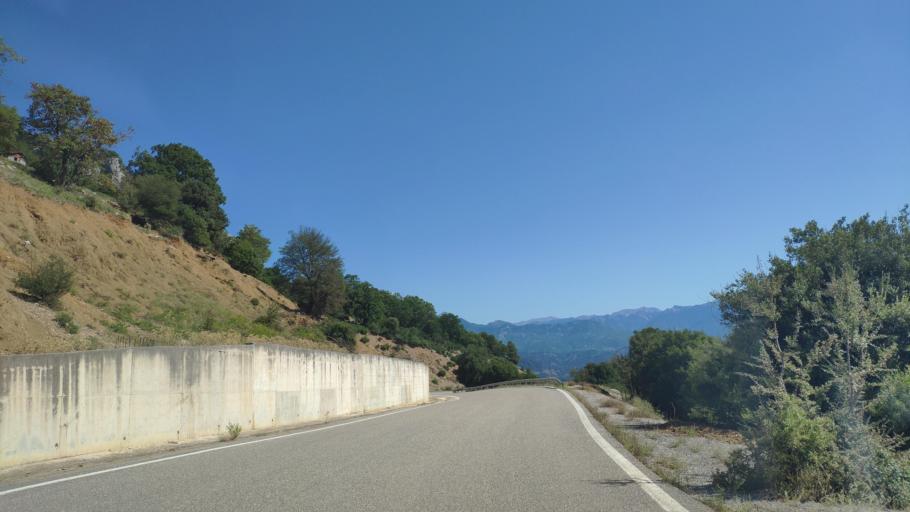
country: GR
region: Central Greece
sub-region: Nomos Evrytanias
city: Kerasochori
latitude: 38.9493
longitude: 21.4638
